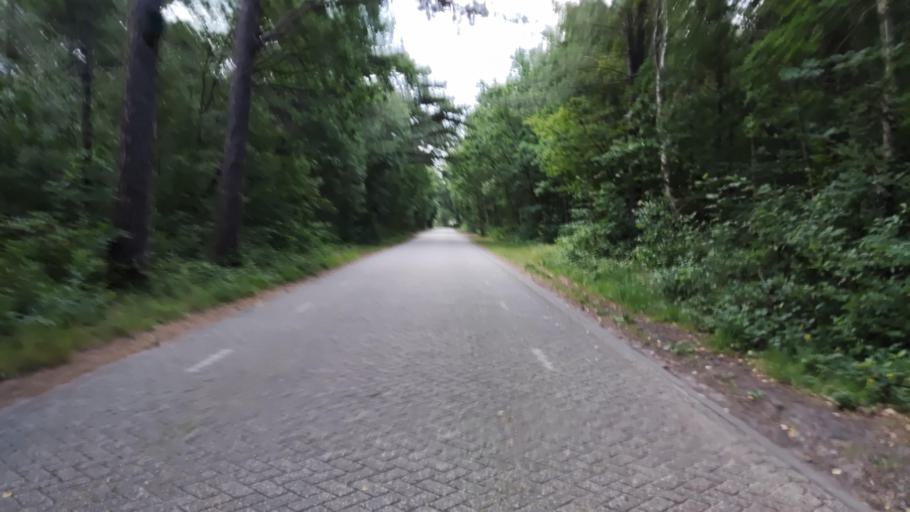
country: NL
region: North Holland
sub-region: Gemeente Texel
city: Den Burg
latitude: 53.0828
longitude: 4.7556
